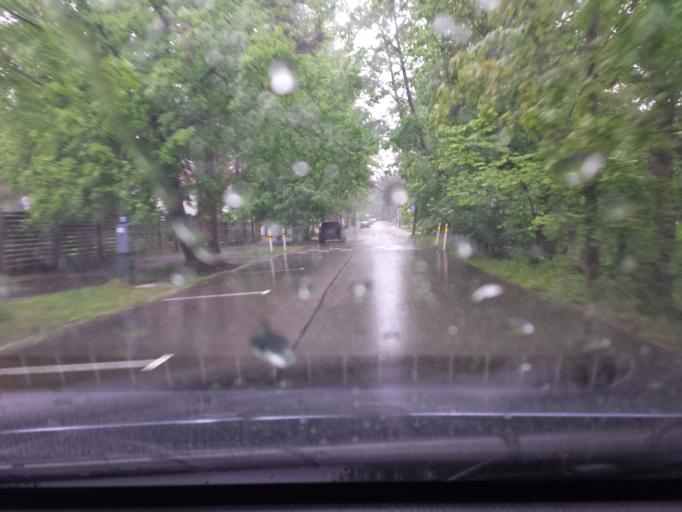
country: LV
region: Riga
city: Bolderaja
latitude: 57.0769
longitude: 24.1121
